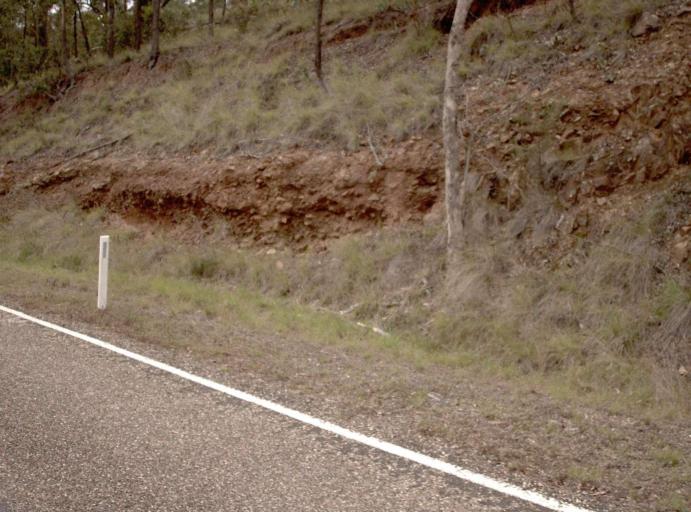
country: AU
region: Victoria
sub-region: East Gippsland
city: Bairnsdale
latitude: -37.5407
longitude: 147.2076
